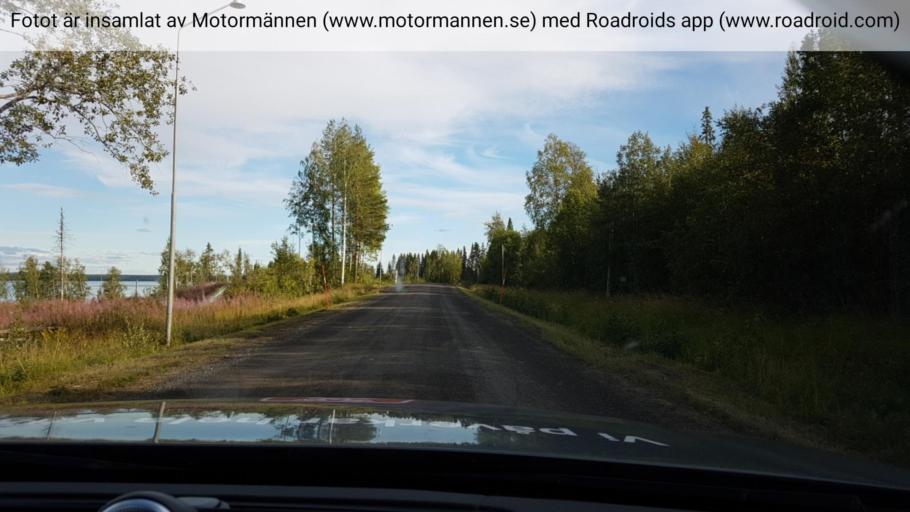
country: SE
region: Jaemtland
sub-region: Stroemsunds Kommun
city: Stroemsund
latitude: 64.1235
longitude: 15.8028
